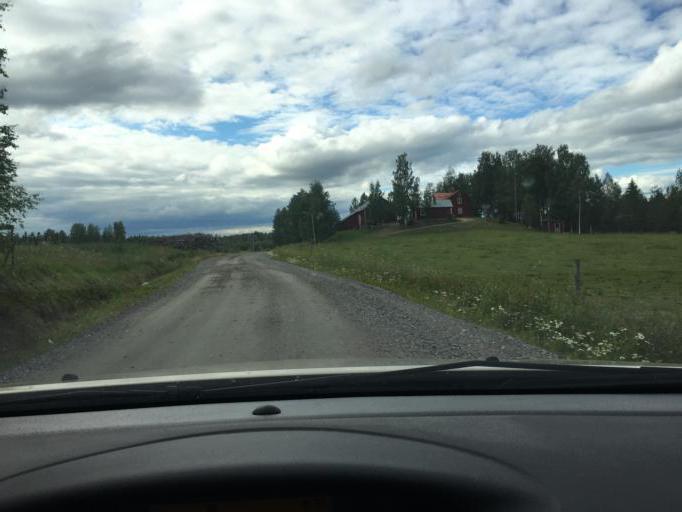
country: SE
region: Norrbotten
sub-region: Overkalix Kommun
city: OEverkalix
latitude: 66.0880
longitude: 22.8876
